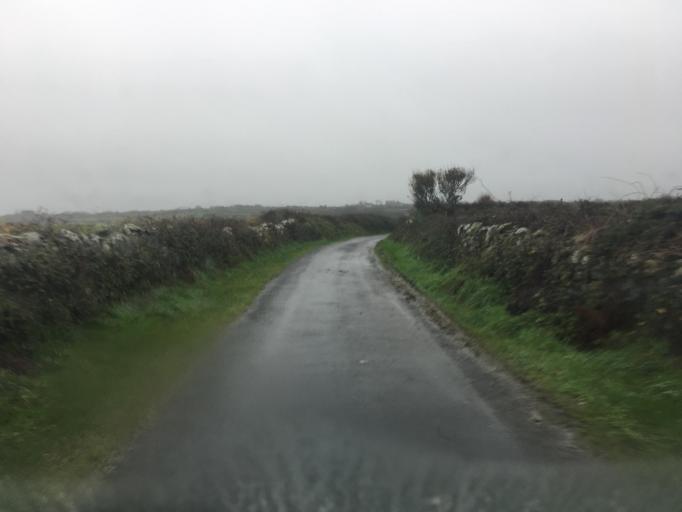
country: FR
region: Lower Normandy
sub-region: Departement de la Manche
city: Beaumont-Hague
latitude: 49.7200
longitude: -1.9206
